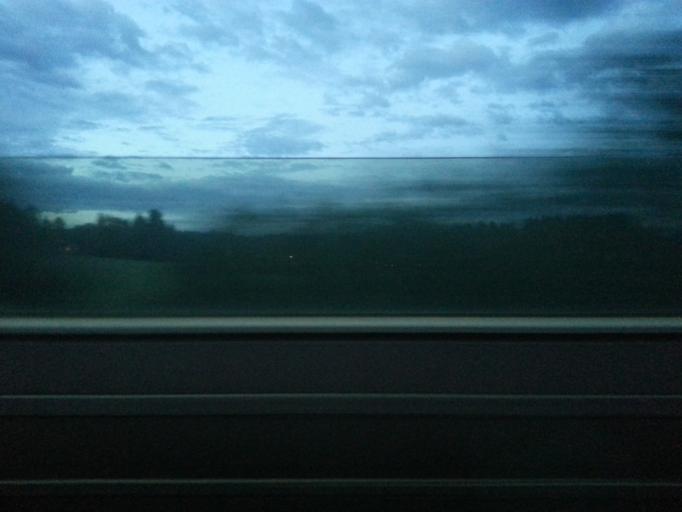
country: NO
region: Akershus
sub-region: Sorum
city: Frogner
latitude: 60.0320
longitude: 11.1259
